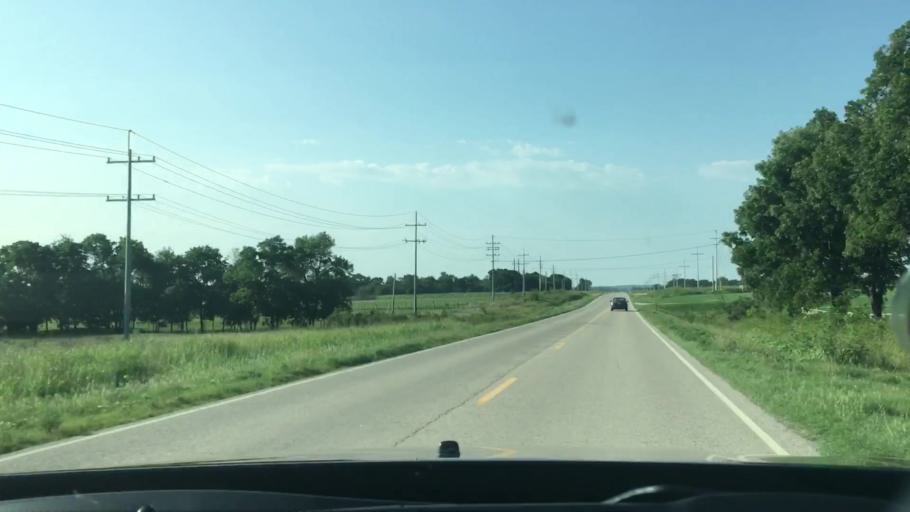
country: US
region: Oklahoma
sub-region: Pontotoc County
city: Ada
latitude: 34.6581
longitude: -96.6349
